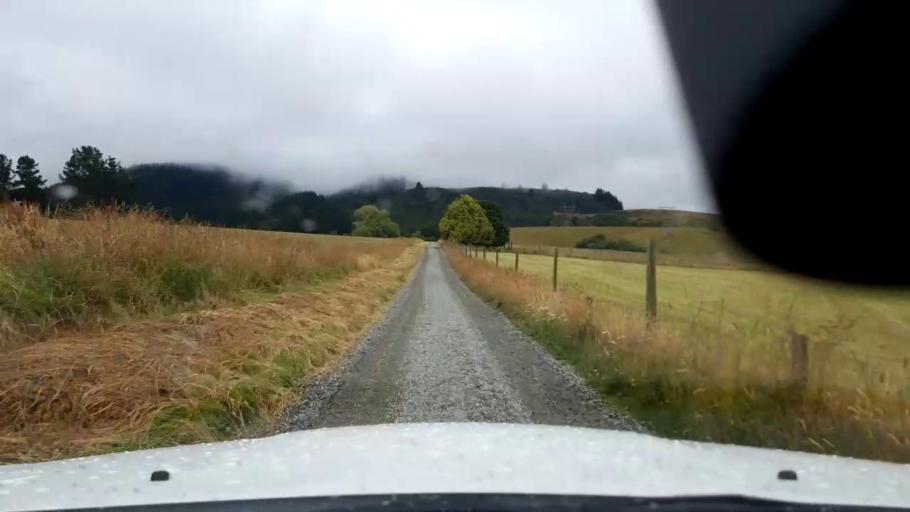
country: NZ
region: Canterbury
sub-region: Timaru District
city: Pleasant Point
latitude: -44.0756
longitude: 171.1457
